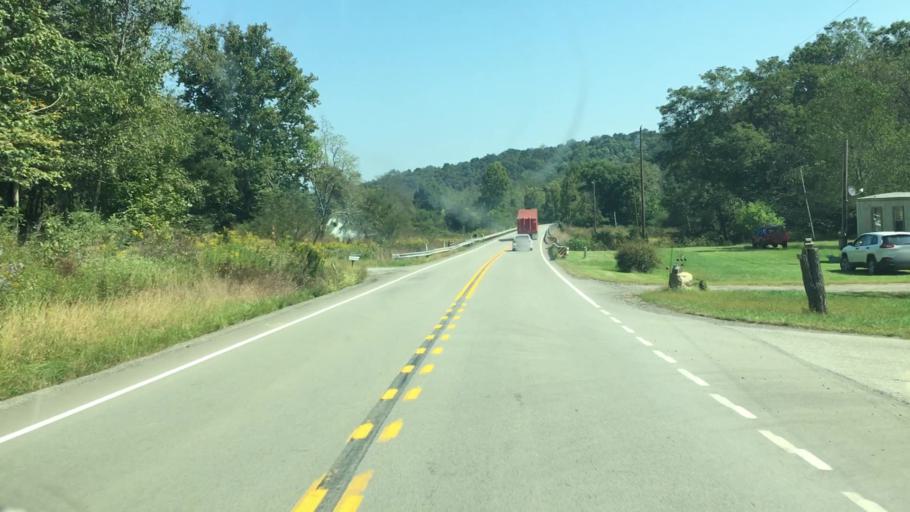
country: US
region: Pennsylvania
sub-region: Washington County
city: Washington
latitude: 40.0297
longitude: -80.2926
